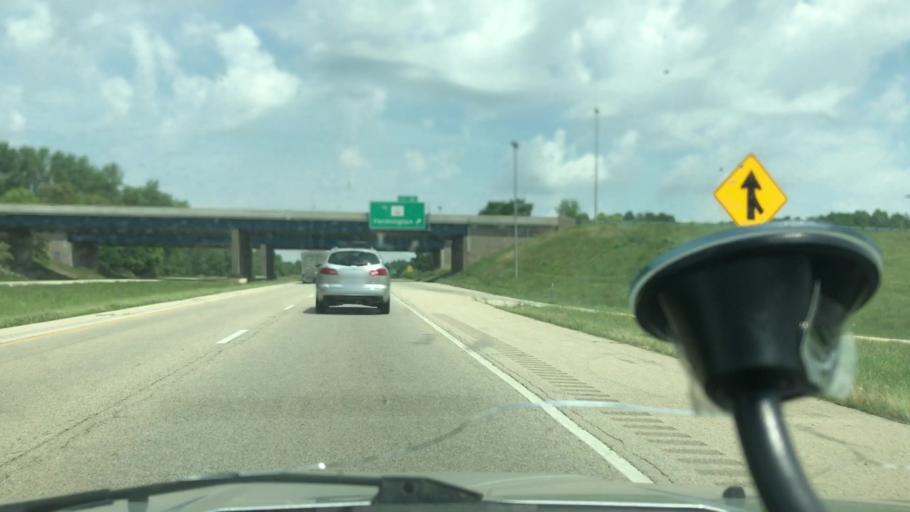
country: US
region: Illinois
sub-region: Peoria County
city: Bellevue
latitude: 40.6928
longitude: -89.6755
